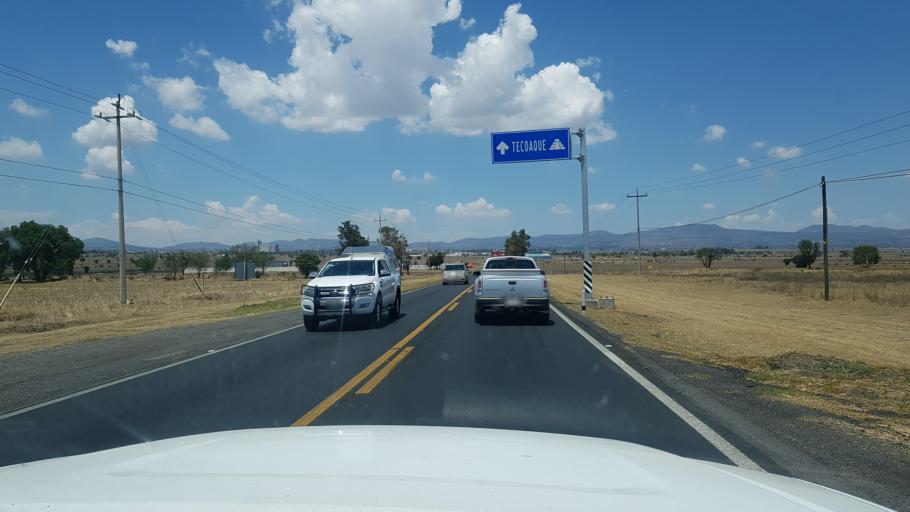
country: MX
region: Hidalgo
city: Calpulalpan
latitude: 19.5761
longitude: -98.5163
